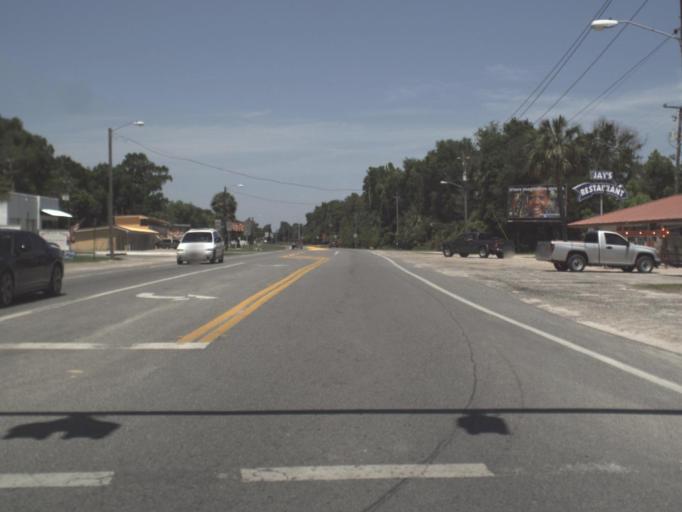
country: US
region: Florida
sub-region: Suwannee County
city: Live Oak
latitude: 30.2997
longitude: -82.9918
